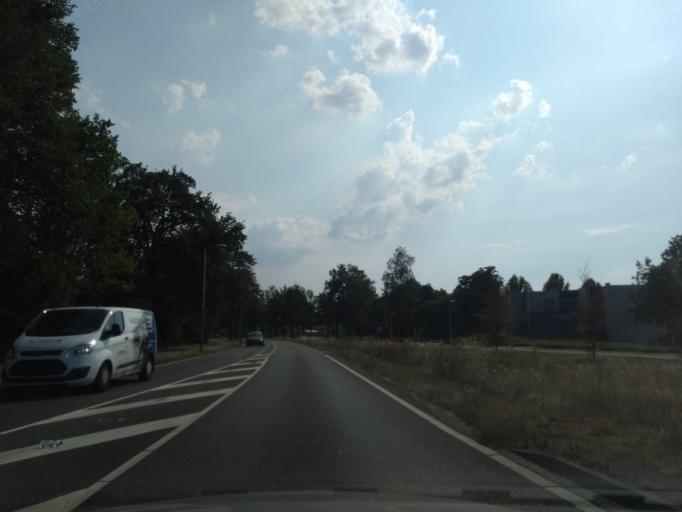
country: NL
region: Gelderland
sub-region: Gemeente Winterswijk
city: Winterswijk
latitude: 51.9802
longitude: 6.7048
